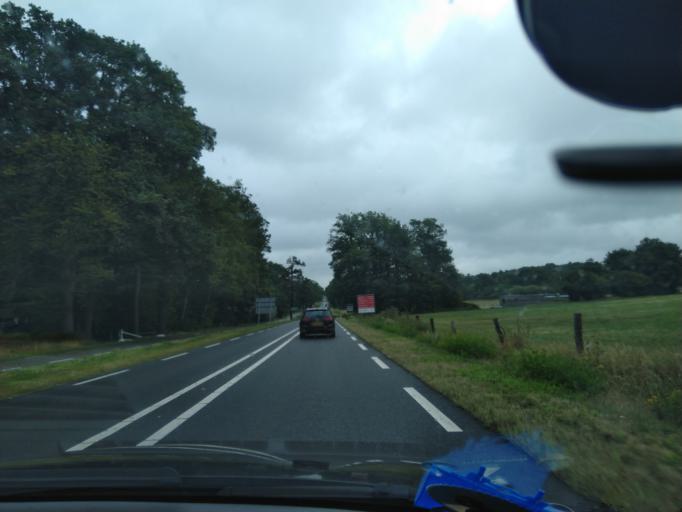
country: NL
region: Overijssel
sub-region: Gemeente Oldenzaal
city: Oldenzaal
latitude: 52.3234
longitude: 6.9420
